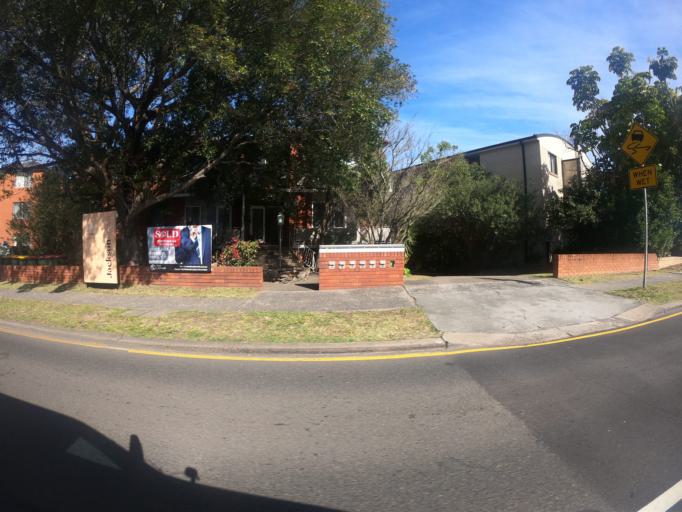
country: AU
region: New South Wales
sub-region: Canada Bay
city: Rhodes
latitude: -33.8167
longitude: 151.1063
